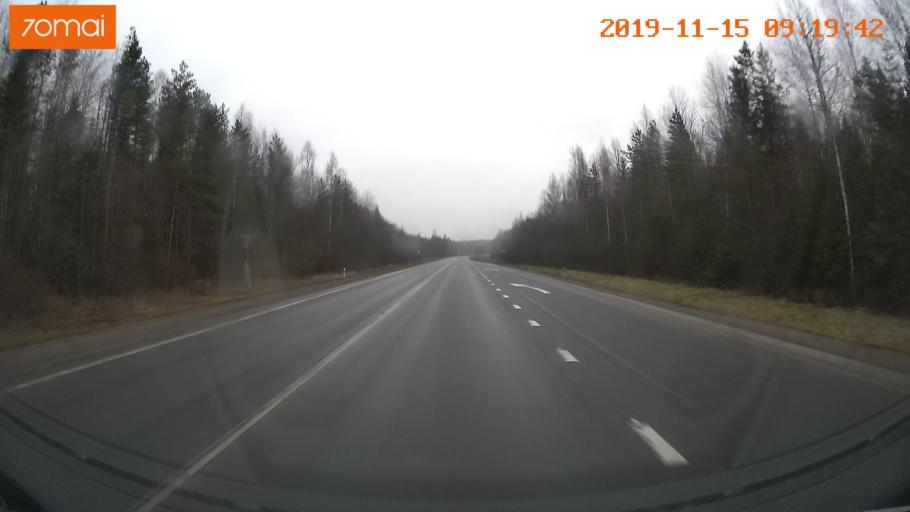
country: RU
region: Vologda
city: Tonshalovo
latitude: 59.2858
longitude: 38.0208
